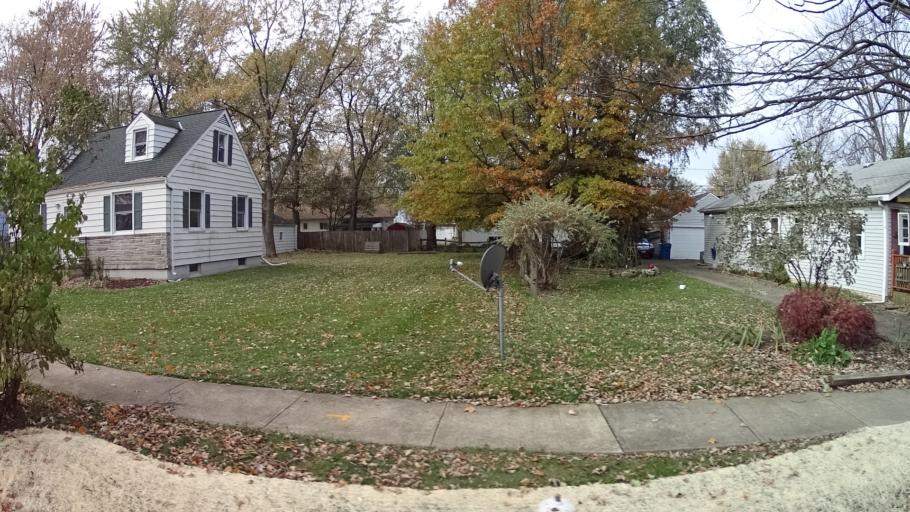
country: US
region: Ohio
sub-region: Lorain County
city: Sheffield Lake
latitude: 41.4862
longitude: -82.1142
